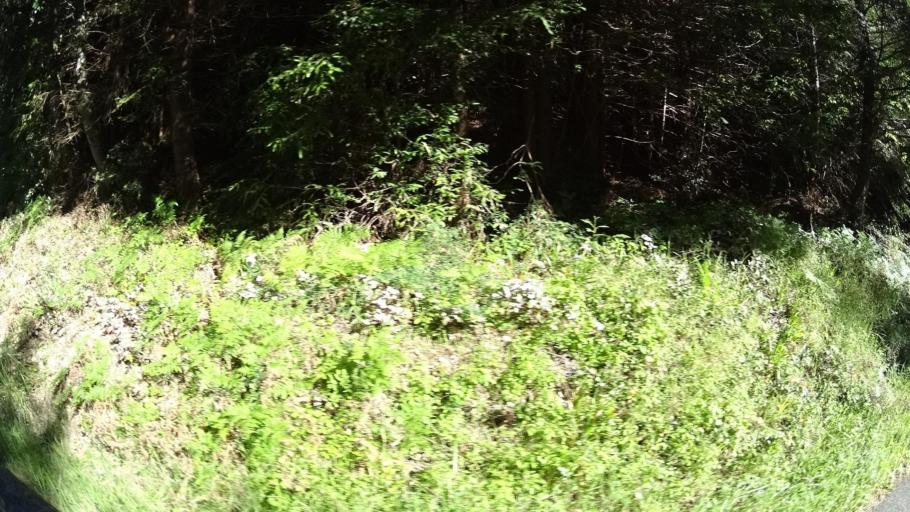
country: US
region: California
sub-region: Humboldt County
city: Rio Dell
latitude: 40.4585
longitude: -124.0014
